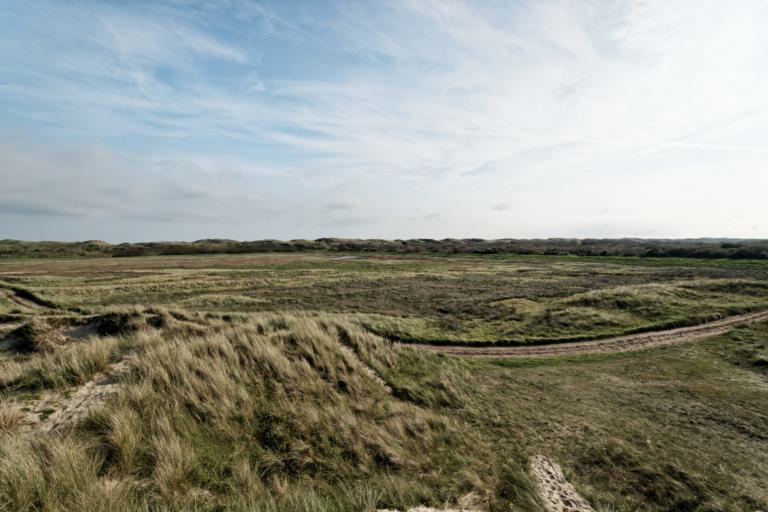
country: NL
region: North Holland
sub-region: Gemeente Texel
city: Den Burg
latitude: 53.1309
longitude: 4.8084
